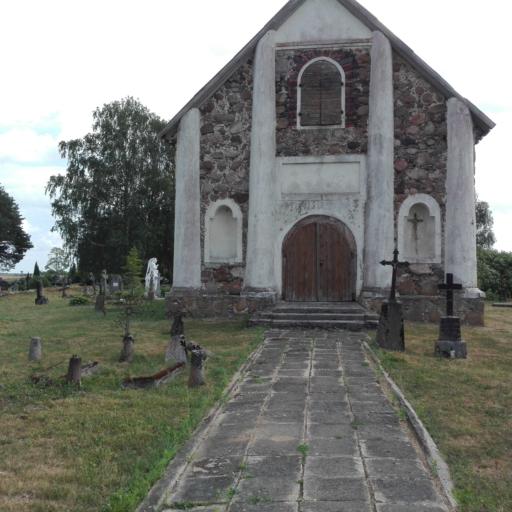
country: LT
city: Obeliai
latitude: 56.1420
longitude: 25.0449
